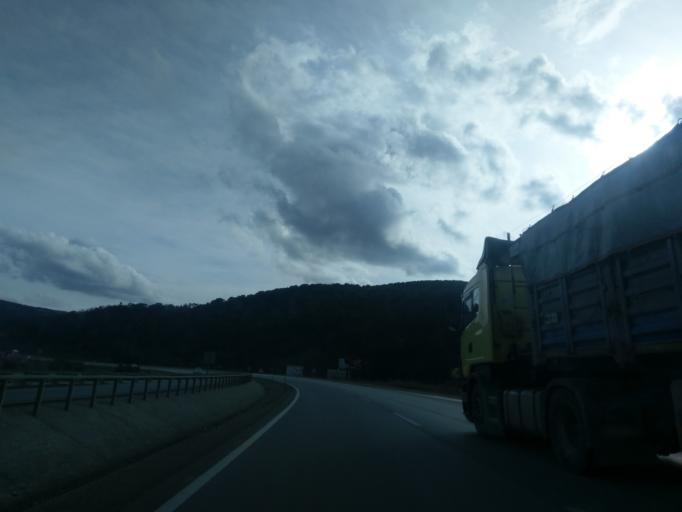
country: TR
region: Kuetahya
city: Sabuncu
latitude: 39.5673
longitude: 30.0718
